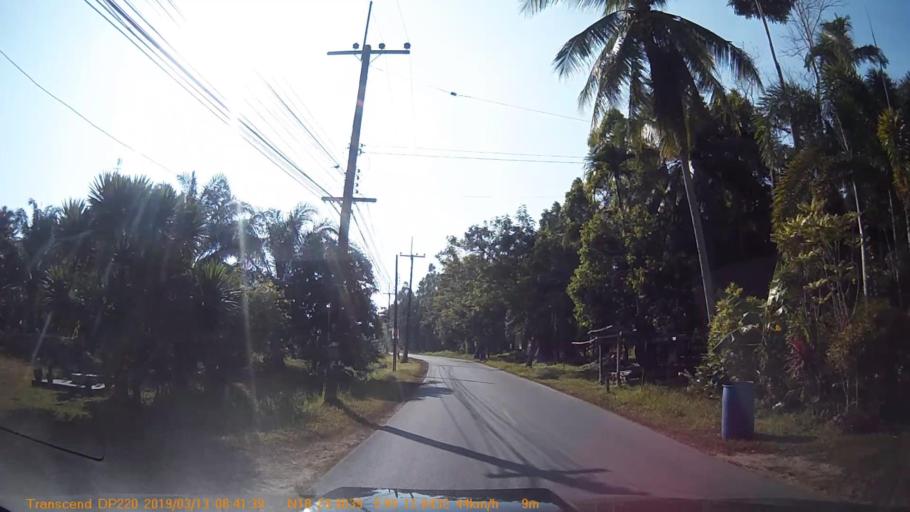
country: TH
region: Chumphon
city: Chumphon
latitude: 10.4986
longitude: 99.2139
